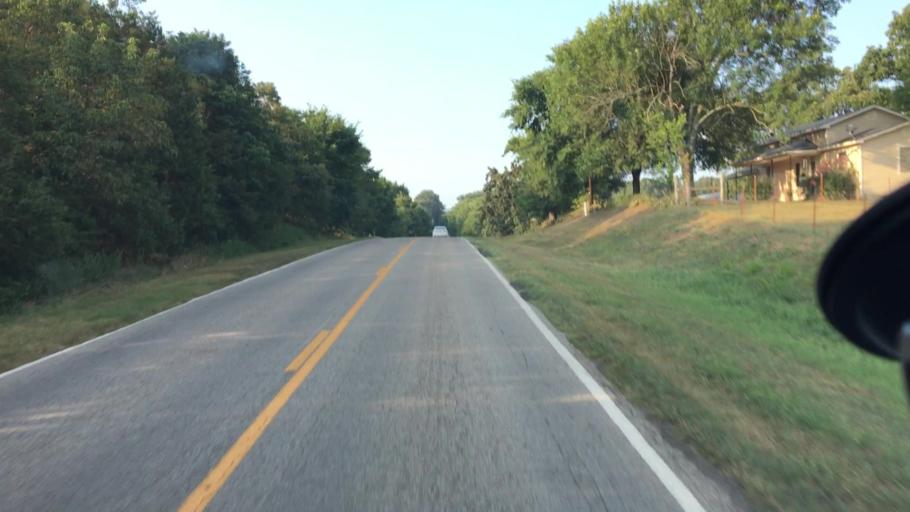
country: US
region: Arkansas
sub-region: Logan County
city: Paris
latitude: 35.3182
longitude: -93.6324
